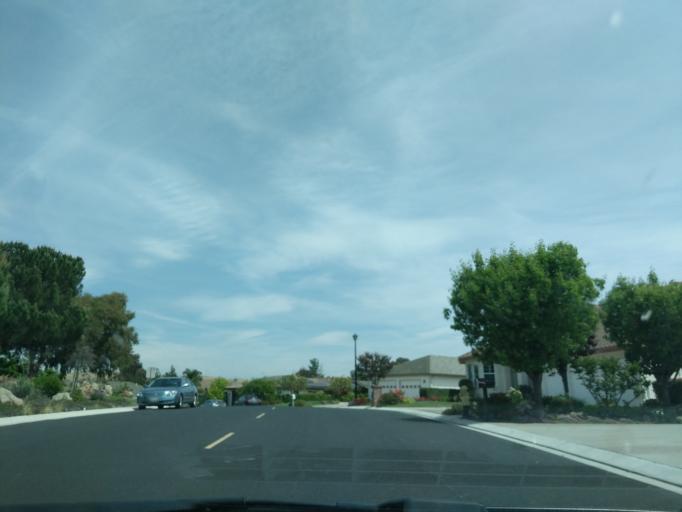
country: US
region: California
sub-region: San Benito County
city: Ridgemark
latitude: 36.8100
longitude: -121.3505
